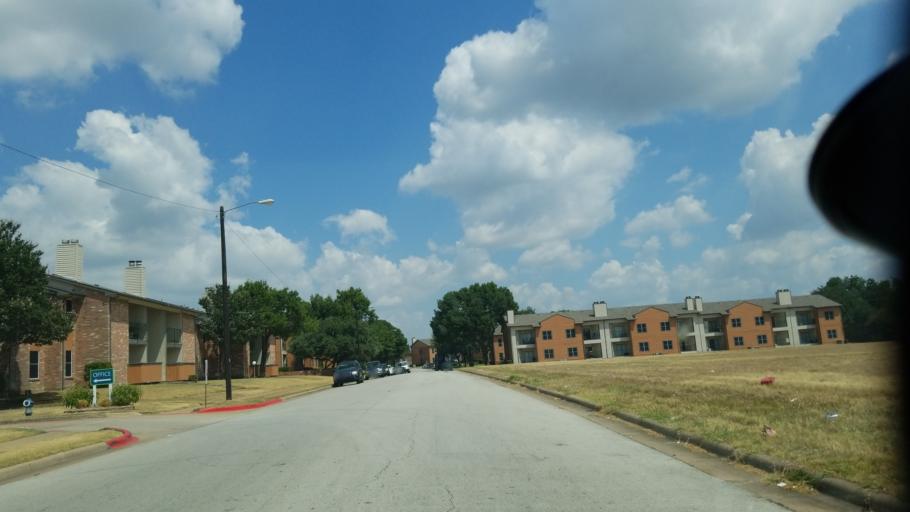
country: US
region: Texas
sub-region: Dallas County
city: Cockrell Hill
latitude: 32.6916
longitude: -96.8874
